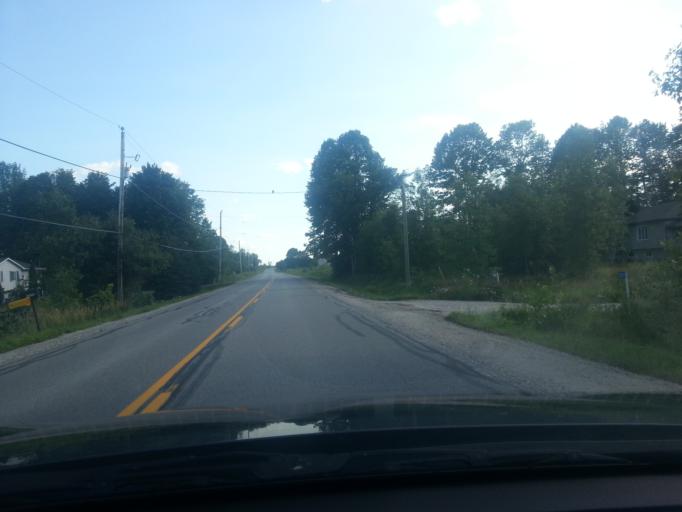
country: CA
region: Ontario
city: Carleton Place
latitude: 45.0865
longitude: -76.2564
